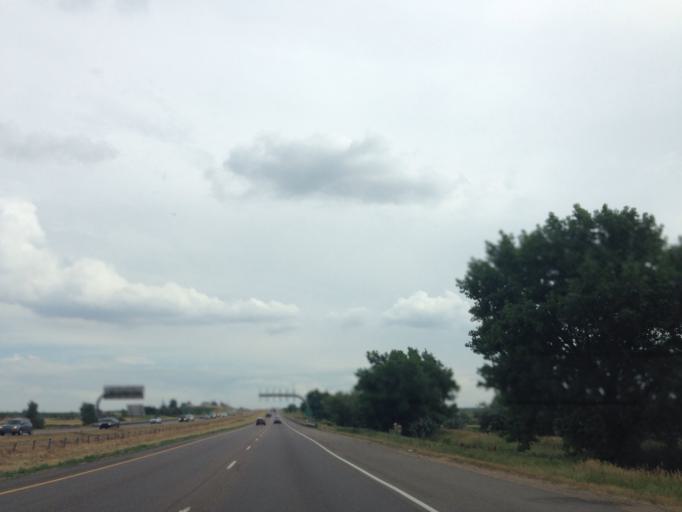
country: US
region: Colorado
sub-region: Larimer County
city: Loveland
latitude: 40.3918
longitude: -104.9935
